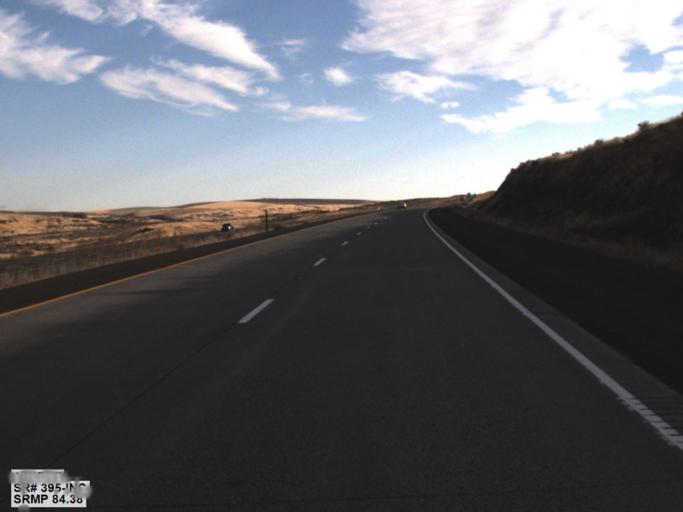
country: US
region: Washington
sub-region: Adams County
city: Ritzville
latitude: 46.9969
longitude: -118.5441
